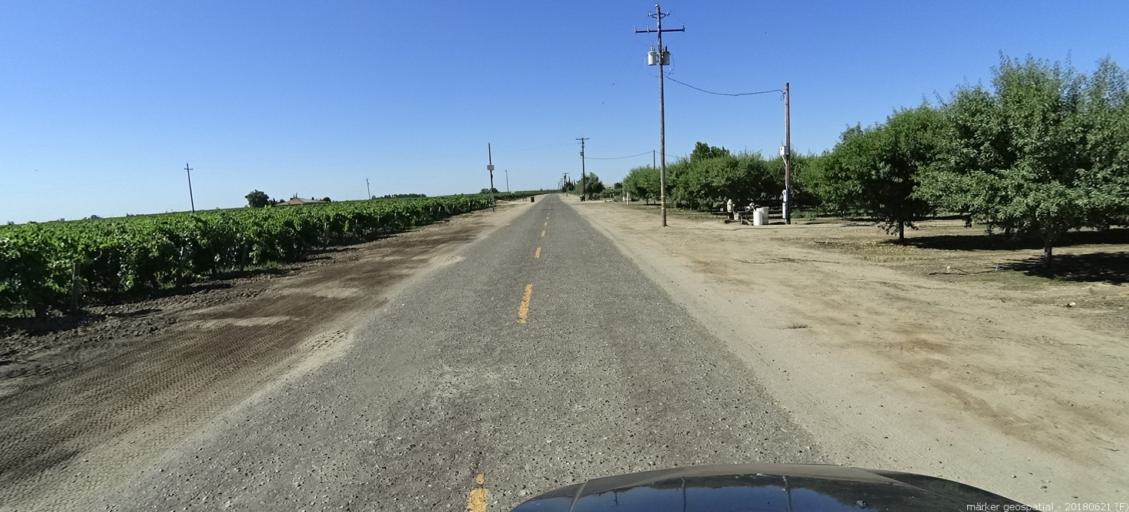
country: US
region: California
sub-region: Fresno County
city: Biola
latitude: 36.8450
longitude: -120.0464
